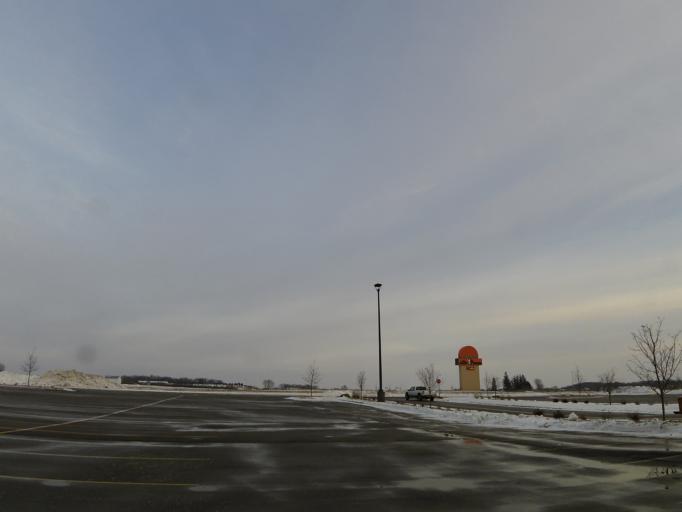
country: US
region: Minnesota
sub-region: Carver County
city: Carver
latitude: 44.7786
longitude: -93.6506
